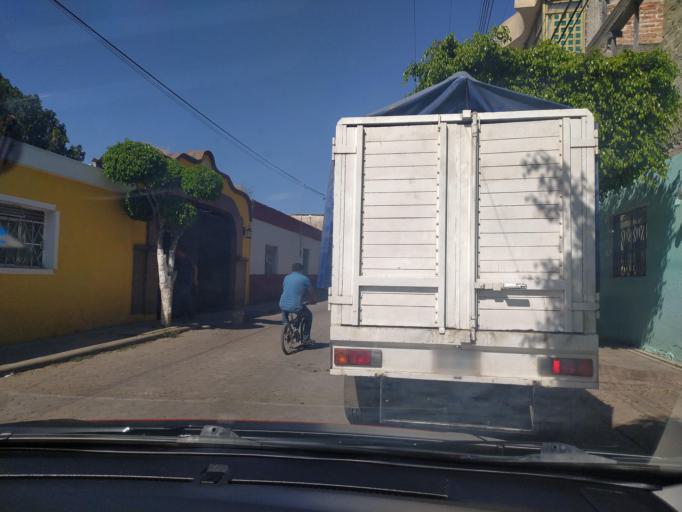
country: MX
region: Jalisco
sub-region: San Pedro Tlaquepaque
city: Paseo del Prado
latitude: 20.5967
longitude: -103.3932
